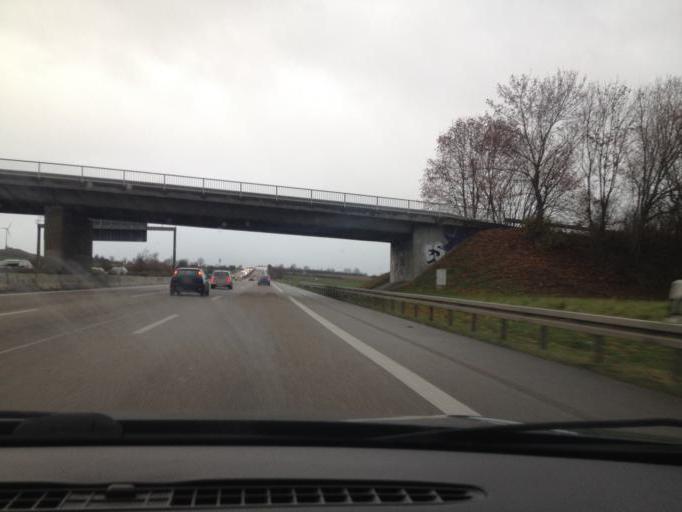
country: DE
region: Baden-Wuerttemberg
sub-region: Regierungsbezirk Stuttgart
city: Korntal
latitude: 48.8427
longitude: 9.1107
